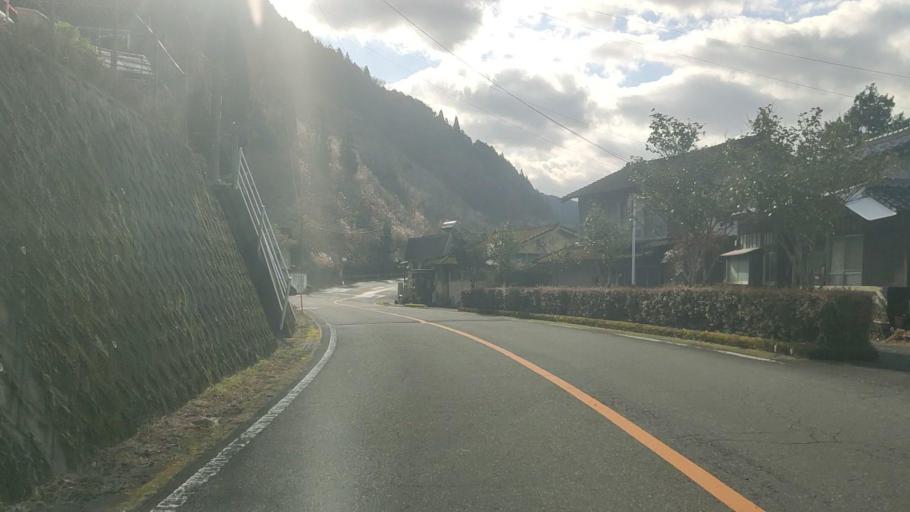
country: JP
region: Kumamoto
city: Hitoyoshi
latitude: 32.3132
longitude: 130.8474
